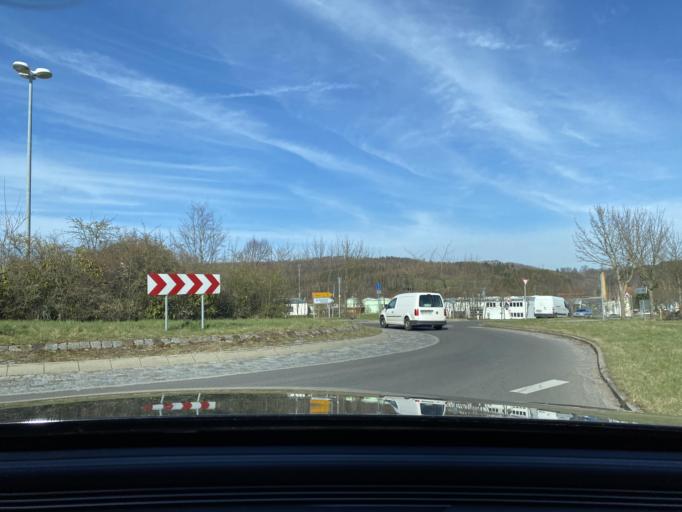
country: DE
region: Saxony
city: Sohland
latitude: 51.0552
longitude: 14.4276
